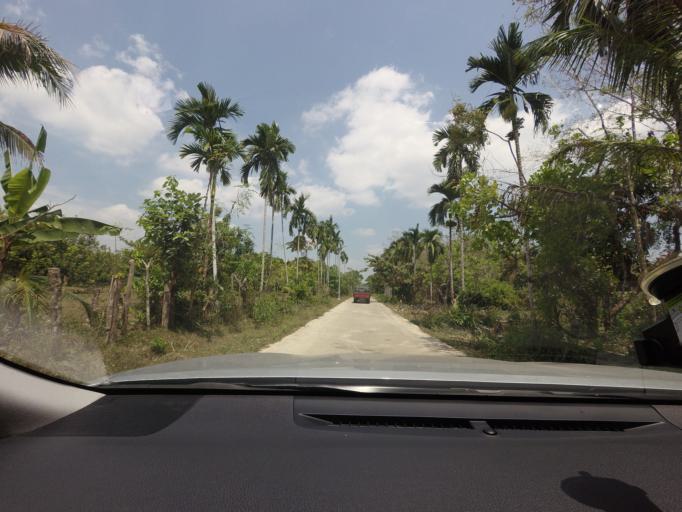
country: TH
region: Narathiwat
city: Rueso
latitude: 6.3847
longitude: 101.4997
